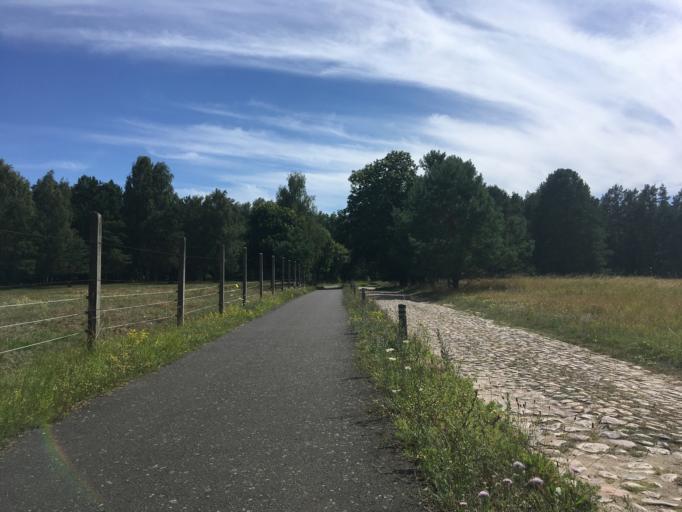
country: DE
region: Brandenburg
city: Rheinsberg
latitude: 53.0803
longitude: 12.9031
